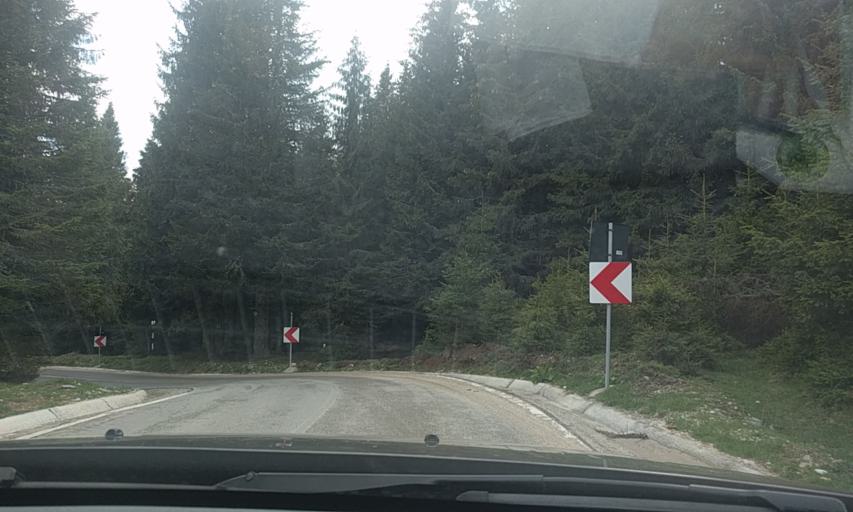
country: RO
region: Prahova
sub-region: Oras Busteni
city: Busteni
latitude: 45.3854
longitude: 25.4383
